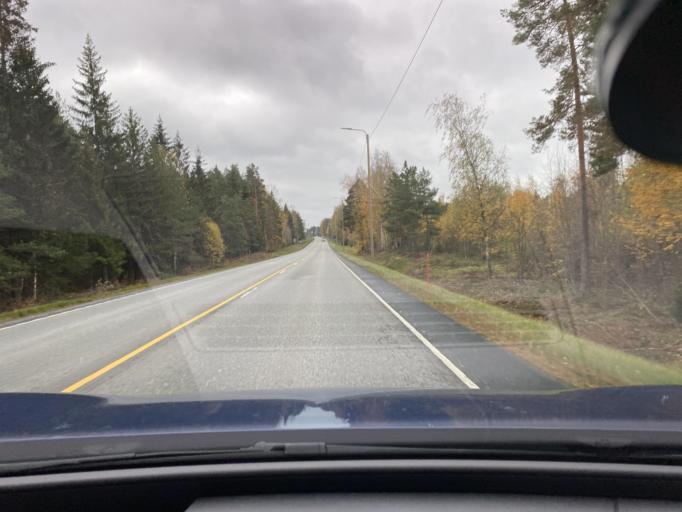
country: FI
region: Varsinais-Suomi
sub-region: Vakka-Suomi
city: Laitila
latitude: 60.9654
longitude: 21.5942
